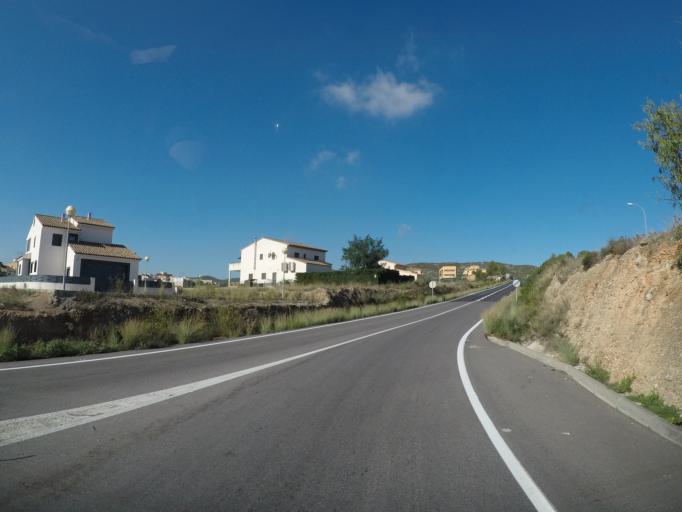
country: ES
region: Catalonia
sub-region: Provincia de Tarragona
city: El Perello
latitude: 40.8789
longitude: 0.7158
